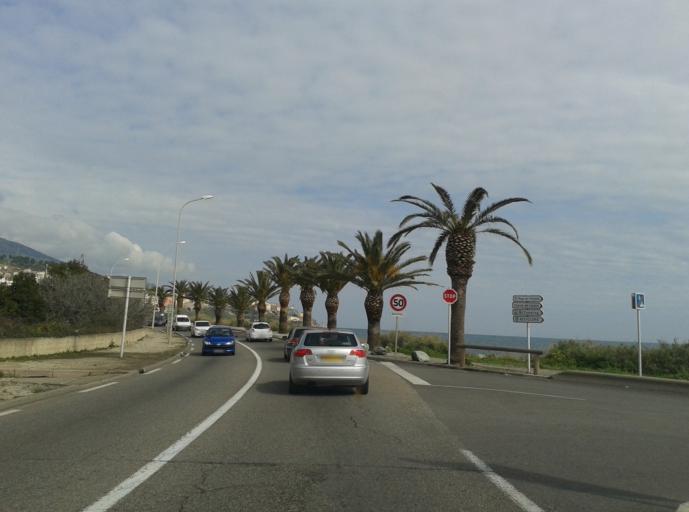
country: FR
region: Corsica
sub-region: Departement de la Haute-Corse
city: Bastia
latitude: 42.6792
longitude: 9.4469
